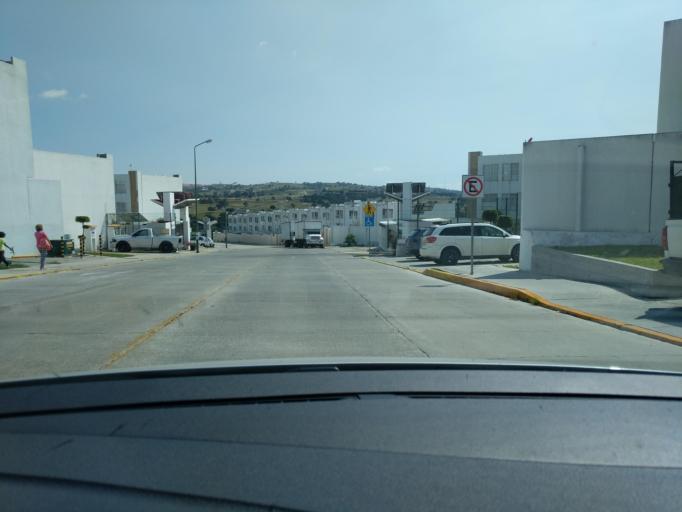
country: MX
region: Puebla
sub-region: Puebla
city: Galaxia la Calera
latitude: 19.0015
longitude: -98.1474
